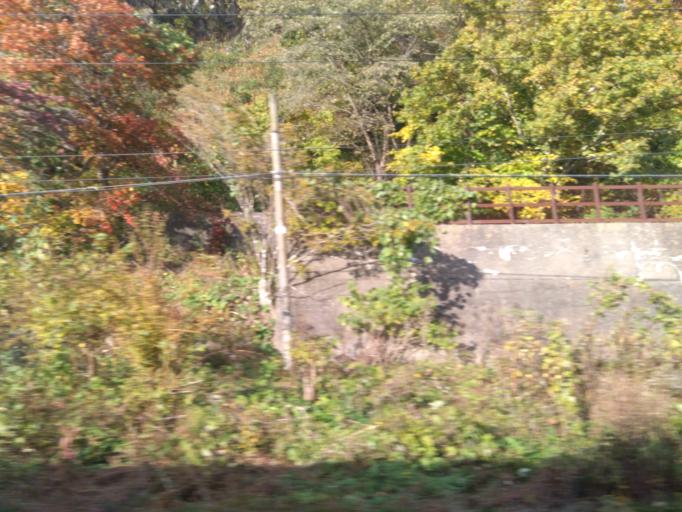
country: JP
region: Hokkaido
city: Niseko Town
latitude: 42.5908
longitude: 140.4732
